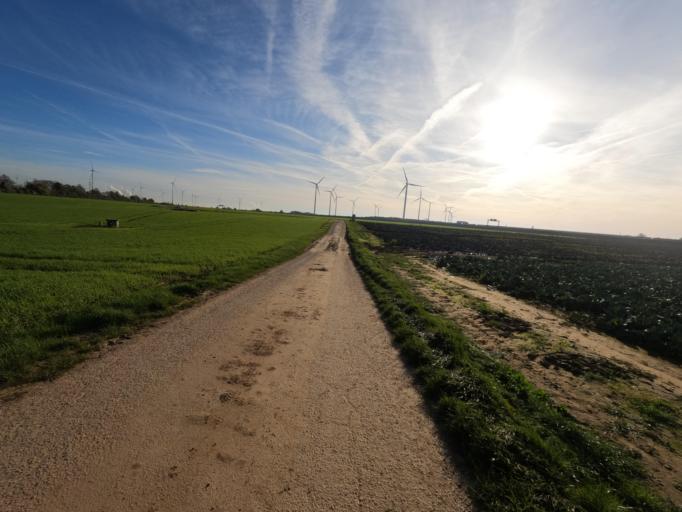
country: DE
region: North Rhine-Westphalia
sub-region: Regierungsbezirk Koln
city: Titz
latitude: 51.0375
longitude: 6.4726
